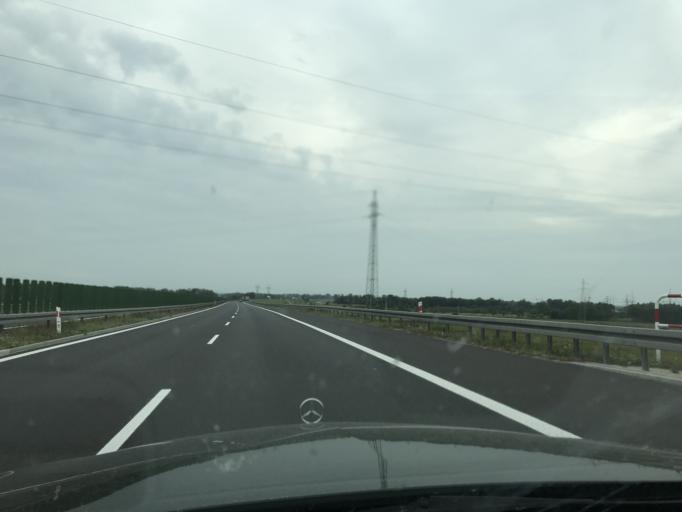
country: PL
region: Lesser Poland Voivodeship
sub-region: Powiat tarnowski
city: Lukowa
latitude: 50.0624
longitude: 20.9557
